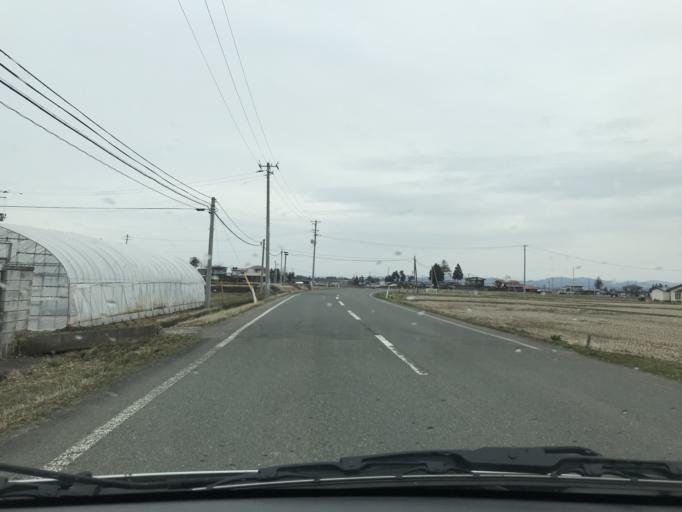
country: JP
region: Iwate
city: Mizusawa
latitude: 39.1700
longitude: 141.1113
